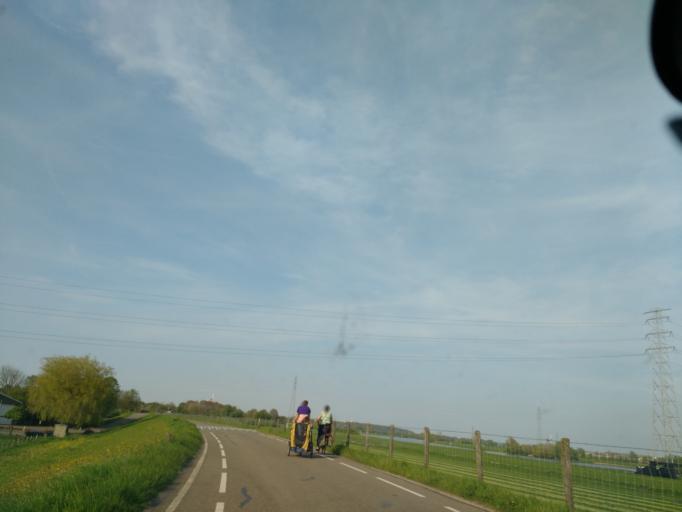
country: NL
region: Gelderland
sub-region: Gemeente Wageningen
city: Wageningen
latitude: 51.9493
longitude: 5.6336
